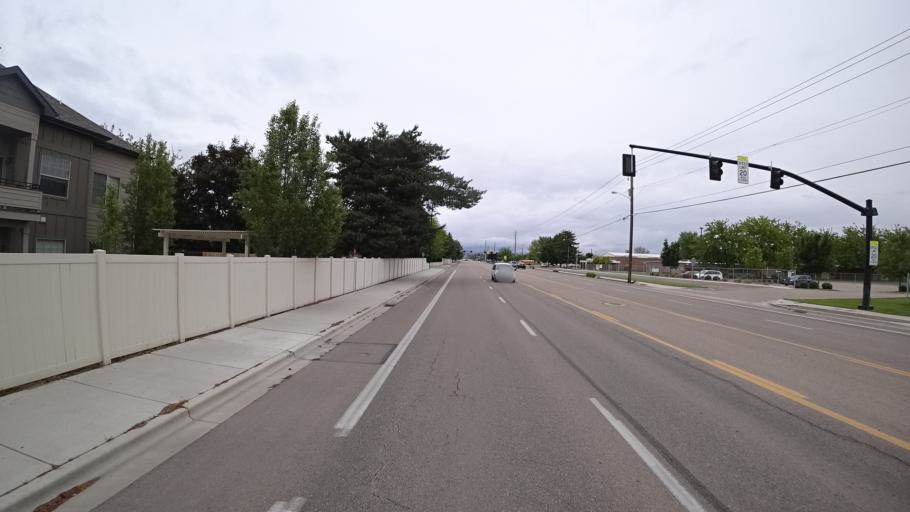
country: US
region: Idaho
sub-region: Ada County
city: Meridian
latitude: 43.6339
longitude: -116.3396
